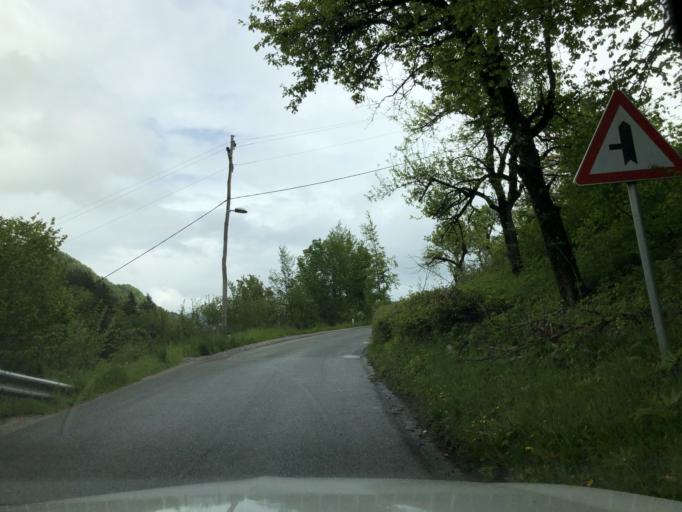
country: SI
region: Gorje
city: Zgornje Gorje
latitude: 46.3891
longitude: 14.0767
